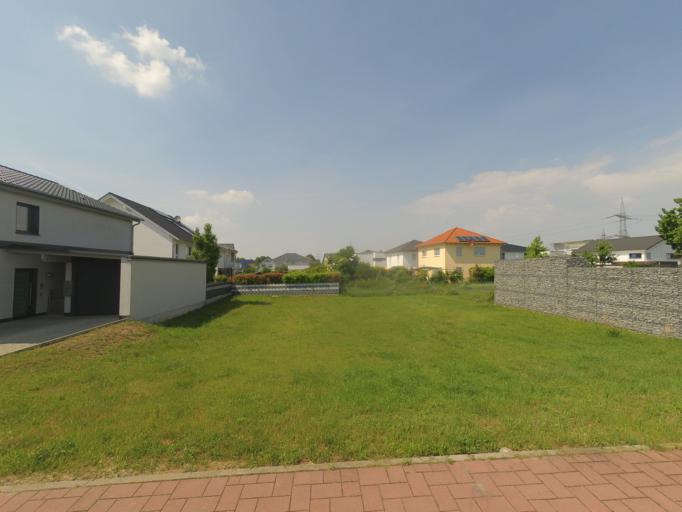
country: DE
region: Hesse
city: Lampertheim
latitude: 49.5937
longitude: 8.4893
